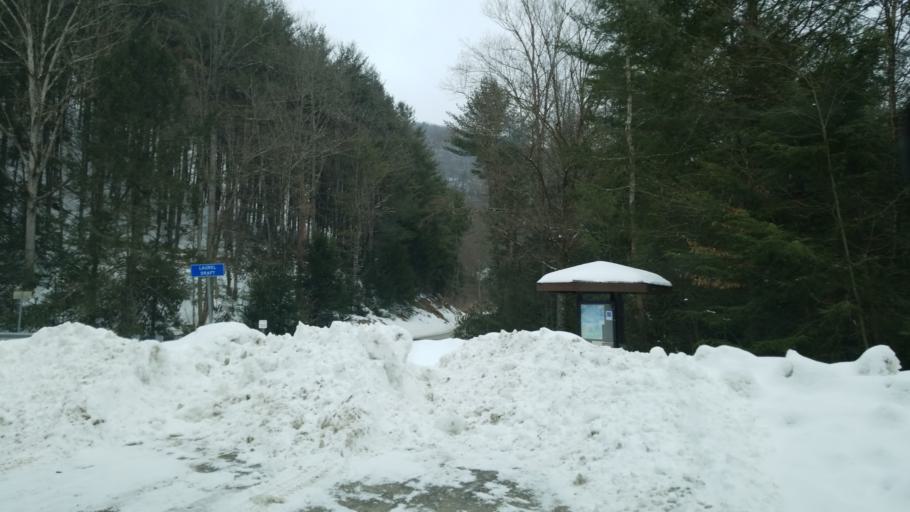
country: US
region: Pennsylvania
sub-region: Cameron County
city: Emporium
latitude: 41.2787
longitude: -78.1401
